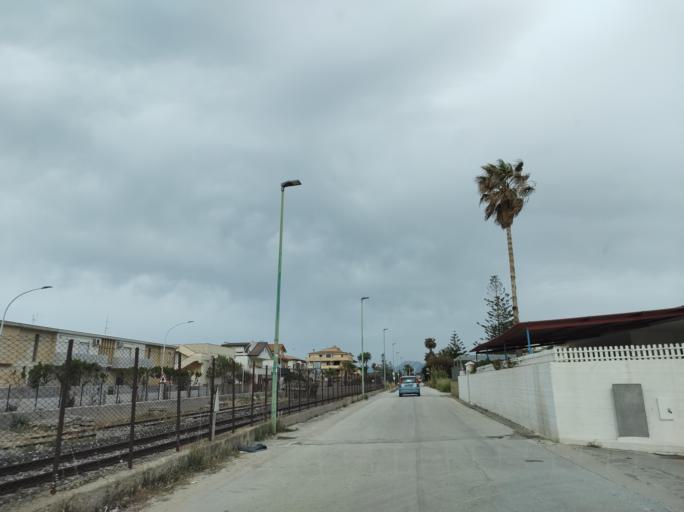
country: IT
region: Sicily
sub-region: Trapani
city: Castellammare del Golfo
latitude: 38.0250
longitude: 12.9178
